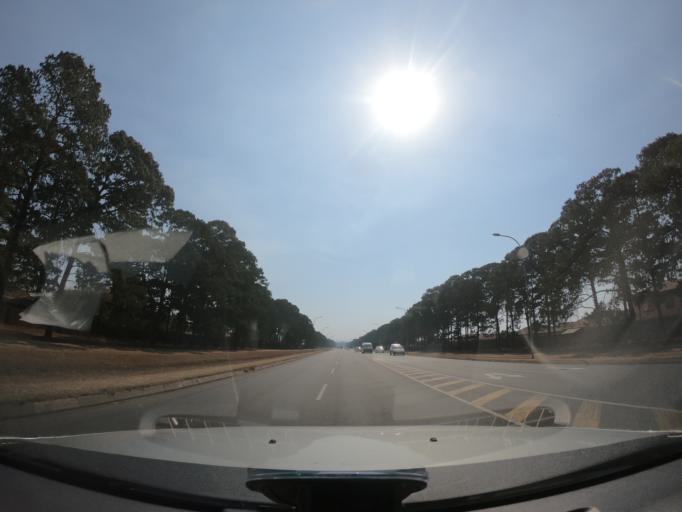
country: ZA
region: Mpumalanga
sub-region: Nkangala District Municipality
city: Middelburg
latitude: -25.8006
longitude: 29.4620
